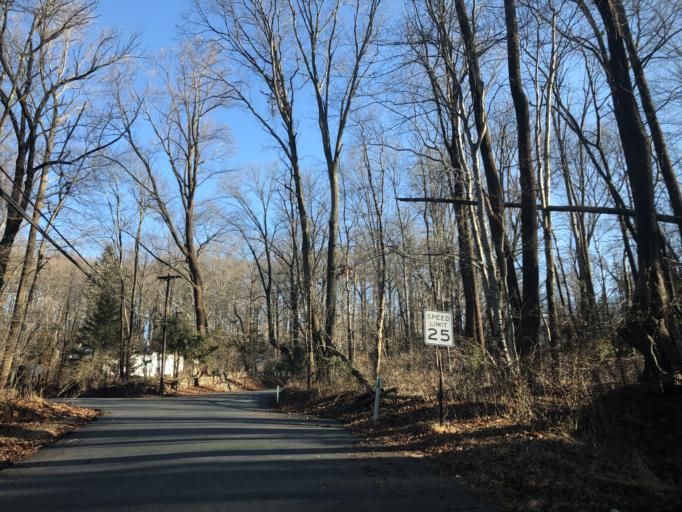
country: US
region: Pennsylvania
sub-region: Delaware County
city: Chester Heights
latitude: 39.9322
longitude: -75.4941
